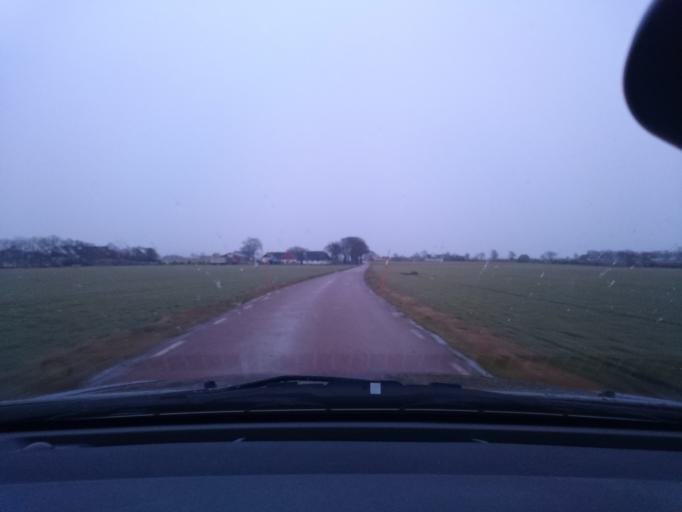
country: SE
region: Skane
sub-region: Angelholms Kommun
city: Vejbystrand
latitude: 56.3446
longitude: 12.7723
